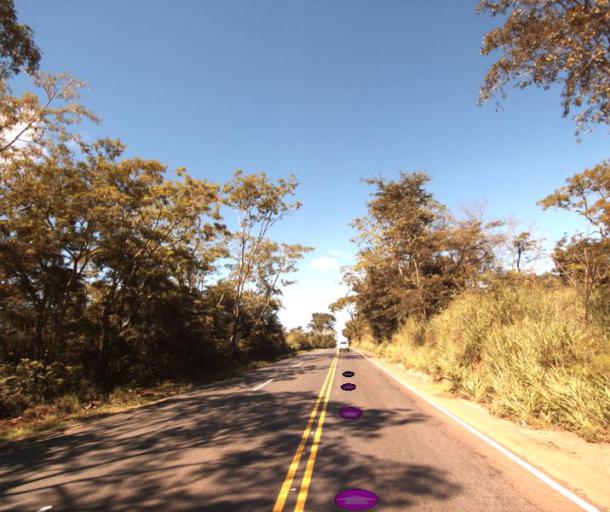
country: BR
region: Goias
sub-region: Ceres
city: Ceres
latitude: -15.1594
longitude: -49.5396
